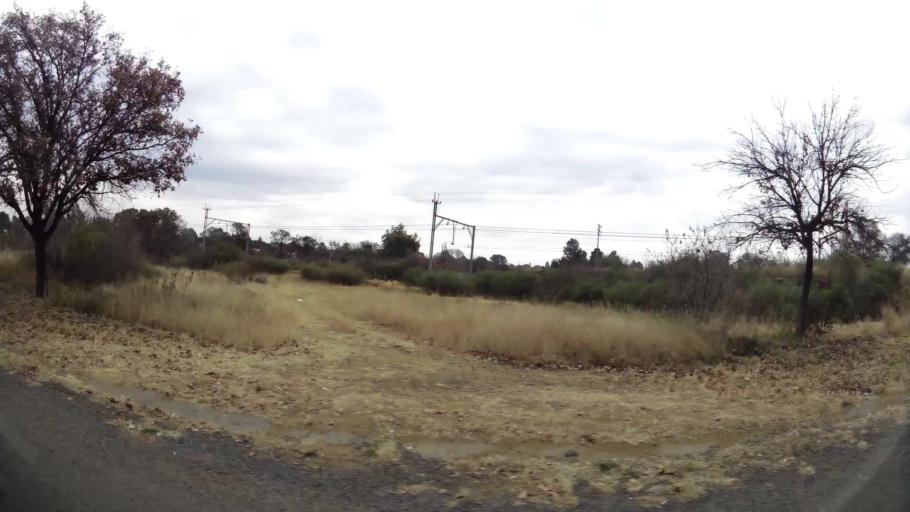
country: ZA
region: Orange Free State
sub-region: Fezile Dabi District Municipality
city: Kroonstad
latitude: -27.6486
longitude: 27.2446
